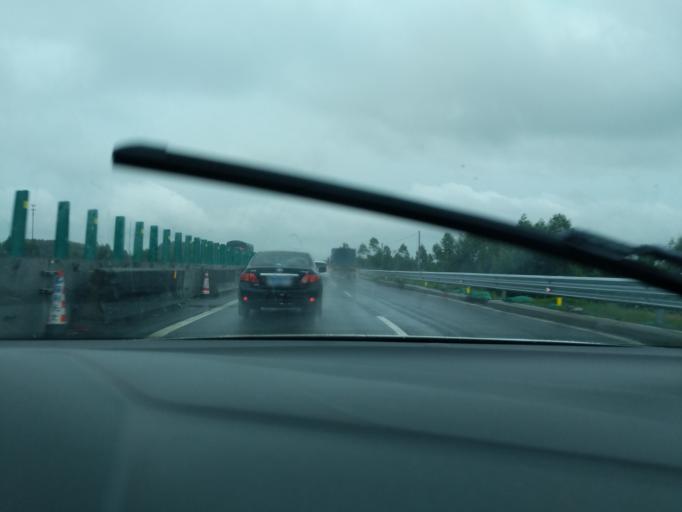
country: CN
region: Guangdong
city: Yueshan
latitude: 22.4627
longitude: 112.7296
